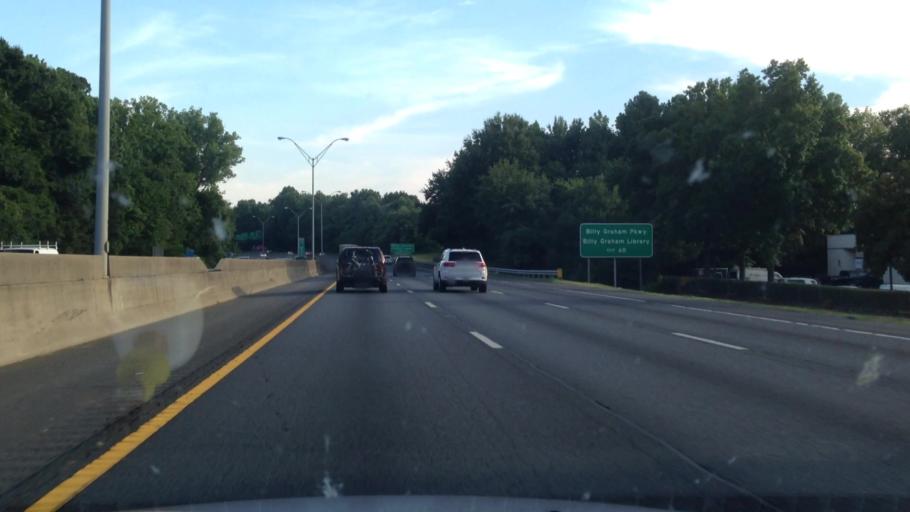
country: US
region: North Carolina
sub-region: Mecklenburg County
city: Charlotte
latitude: 35.1890
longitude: -80.8870
